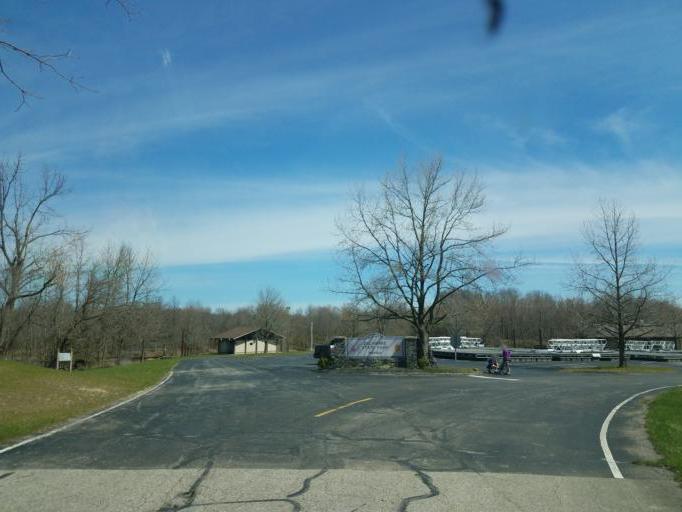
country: US
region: Ohio
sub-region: Delaware County
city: Delaware
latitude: 40.3831
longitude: -83.0587
